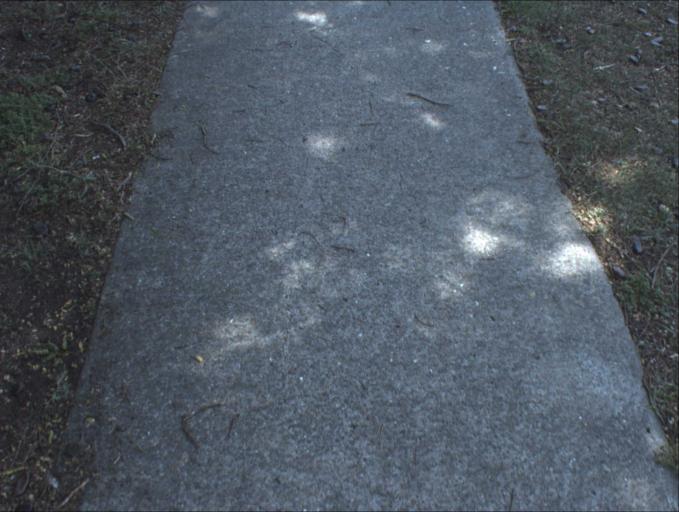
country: AU
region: Queensland
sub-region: Logan
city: Slacks Creek
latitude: -27.6691
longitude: 153.1473
